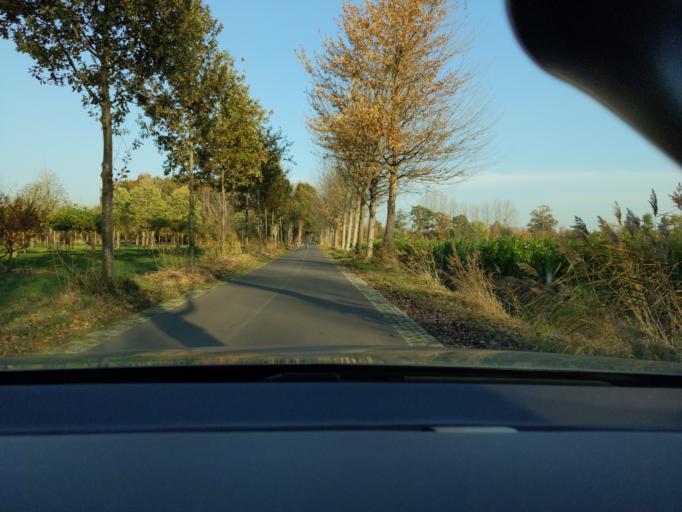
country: NL
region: North Brabant
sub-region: Gemeente Best
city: Best
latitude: 51.5484
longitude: 5.4074
